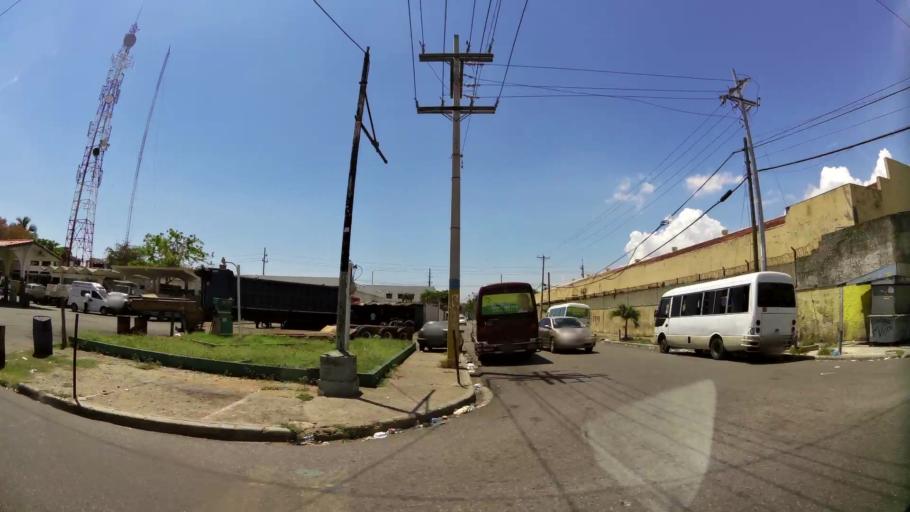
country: DO
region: Nacional
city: Ensanche Luperon
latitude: 18.4939
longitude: -69.8931
